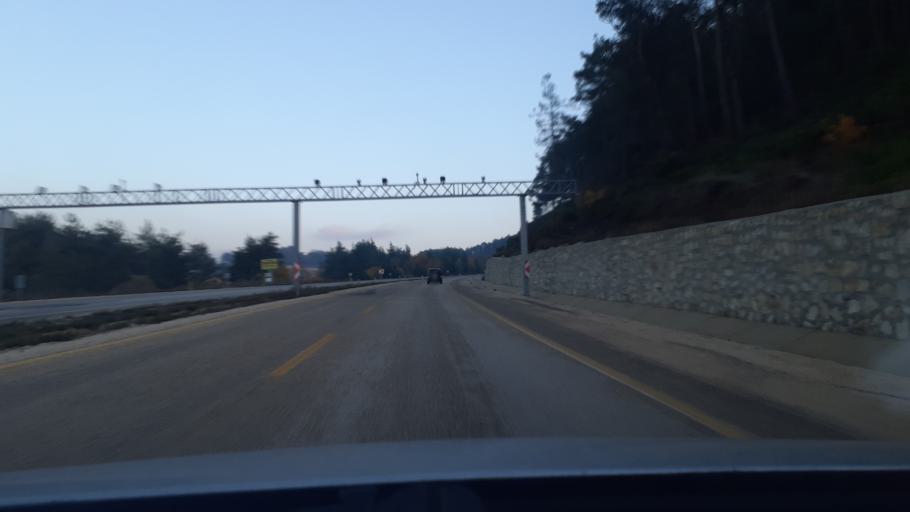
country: TR
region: Hatay
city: Yayladagi
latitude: 35.8948
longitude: 36.0813
